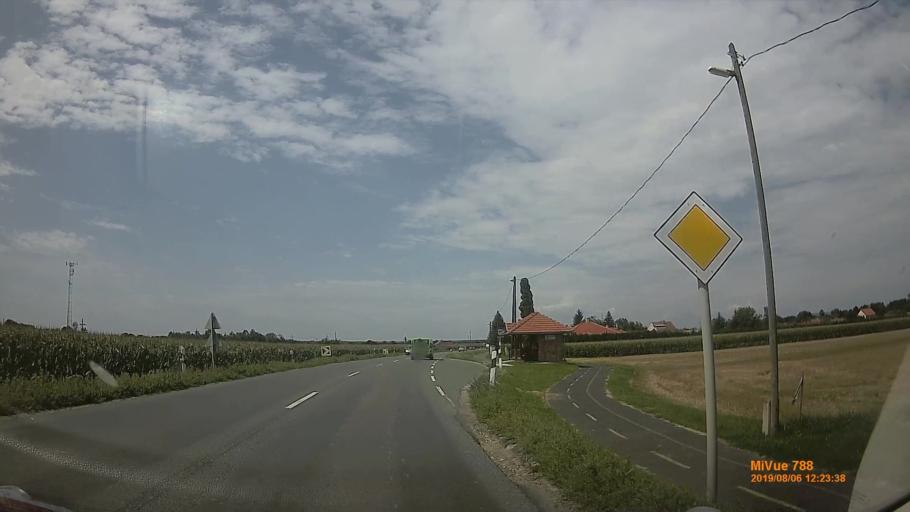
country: HU
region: Vas
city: Taplanszentkereszt
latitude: 47.1905
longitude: 16.7106
